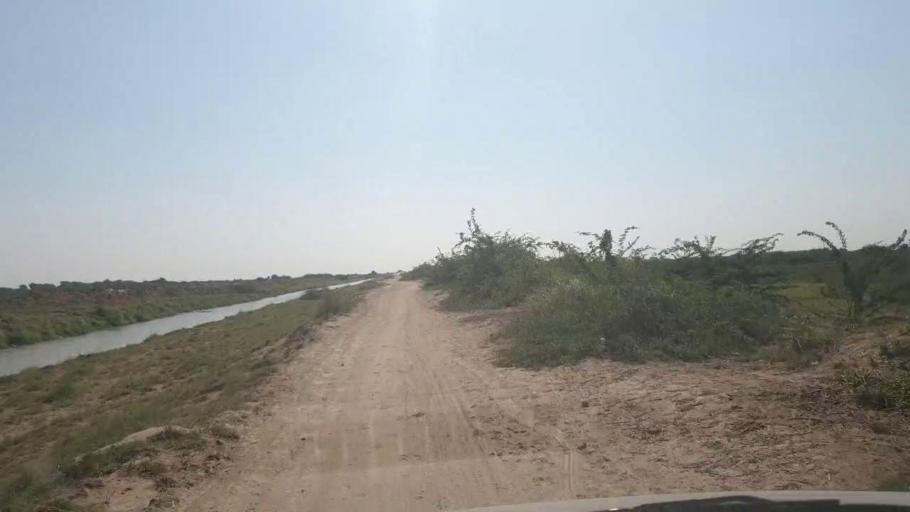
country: PK
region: Sindh
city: Digri
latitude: 24.9267
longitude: 69.1646
